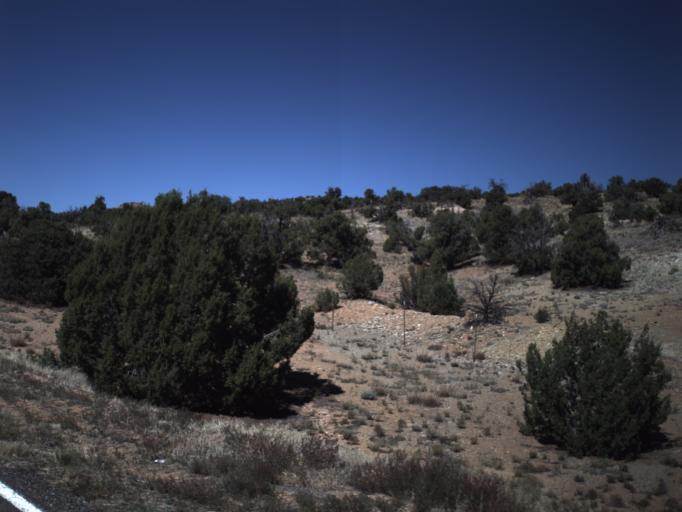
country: US
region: Utah
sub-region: Wayne County
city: Loa
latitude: 37.7369
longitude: -111.5457
